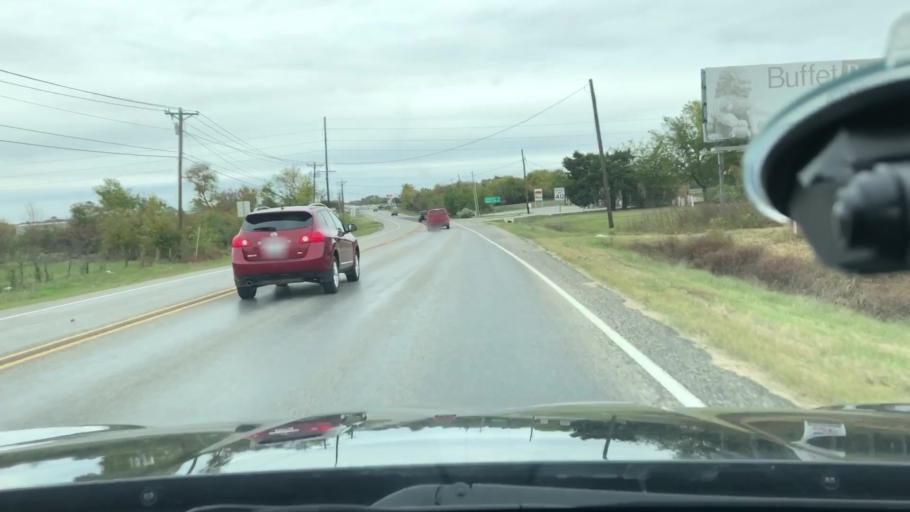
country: US
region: Texas
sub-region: Hunt County
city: Greenville
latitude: 33.0788
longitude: -96.1090
